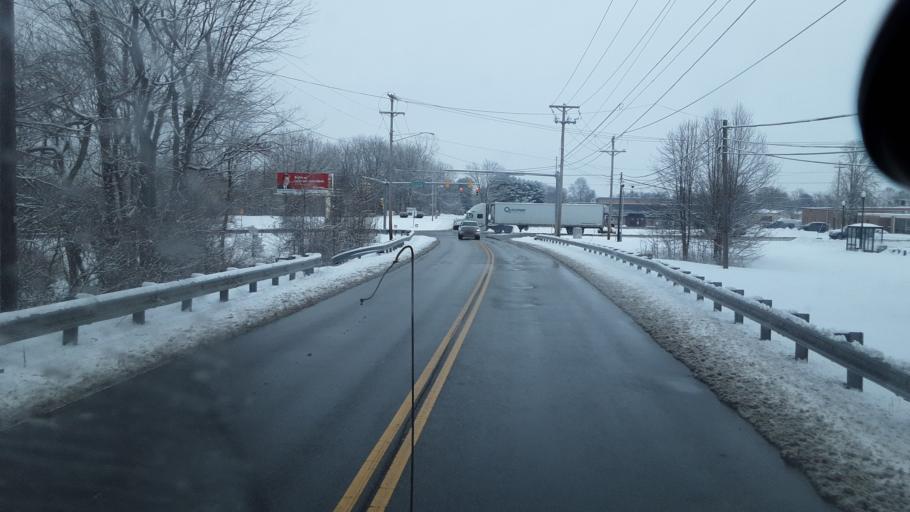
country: US
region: Ohio
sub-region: Licking County
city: Heath
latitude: 40.0468
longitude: -82.4756
